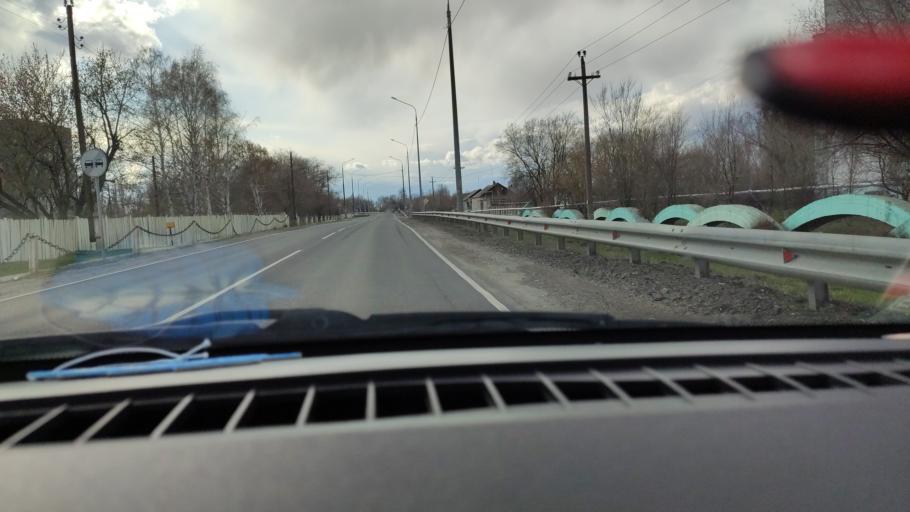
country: RU
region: Saratov
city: Sennoy
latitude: 52.1533
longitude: 46.9524
